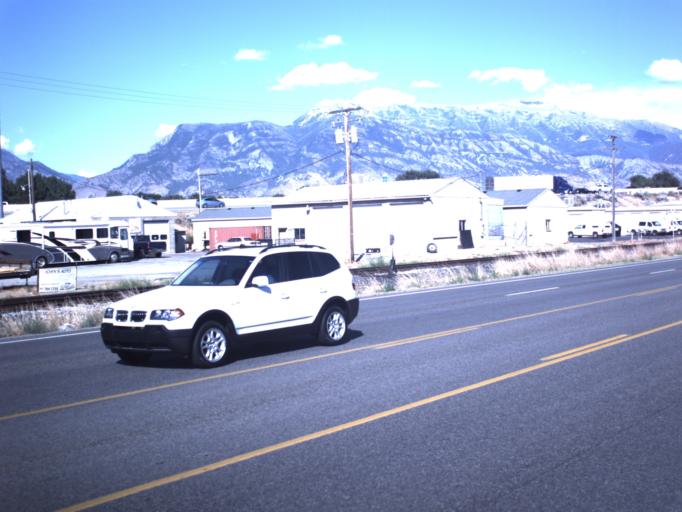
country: US
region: Utah
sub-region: Utah County
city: Lehi
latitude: 40.3936
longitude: -111.8393
